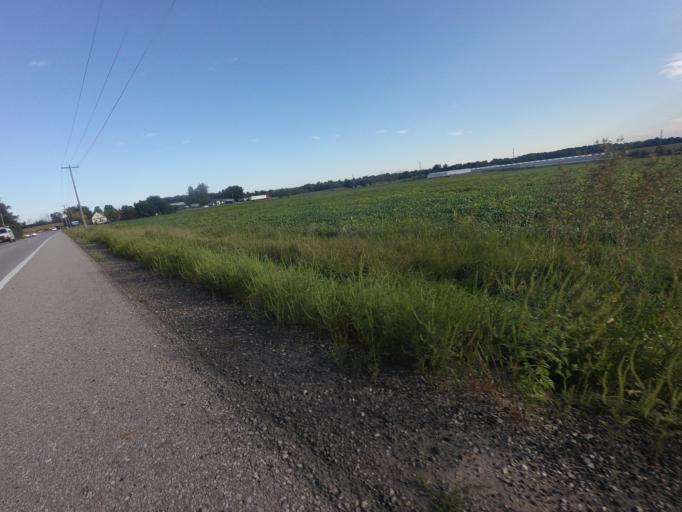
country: CA
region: Ontario
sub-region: Wellington County
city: Guelph
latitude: 43.5884
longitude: -80.3474
